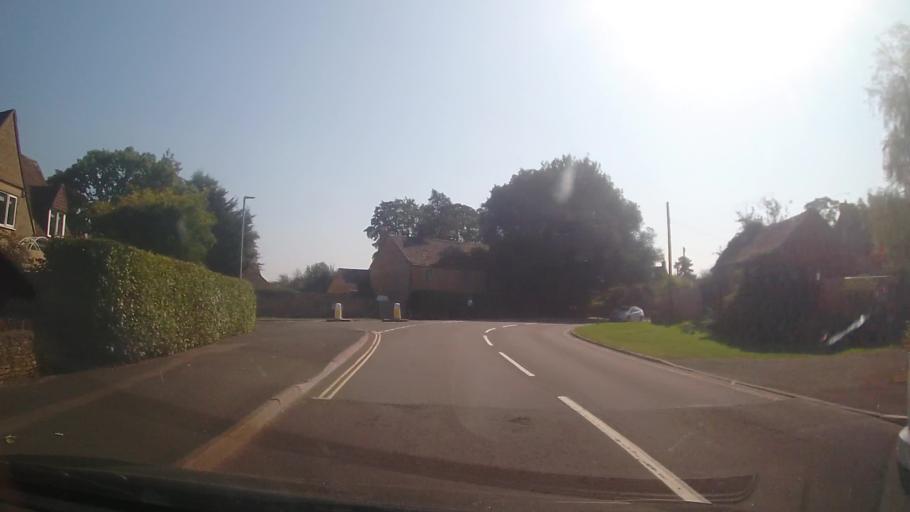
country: GB
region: England
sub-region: Gloucestershire
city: Bourton on the Water
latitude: 51.8866
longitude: -1.7545
